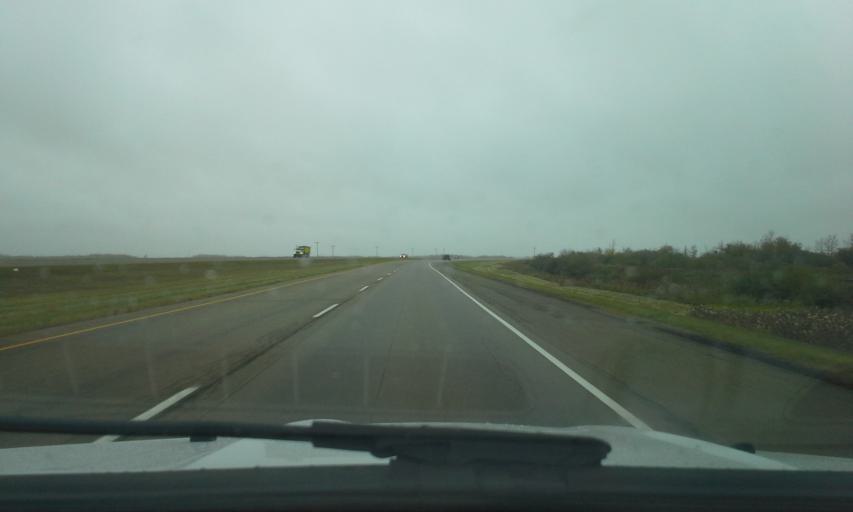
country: CA
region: Saskatchewan
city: Lloydminster
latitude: 53.2283
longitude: -109.8287
